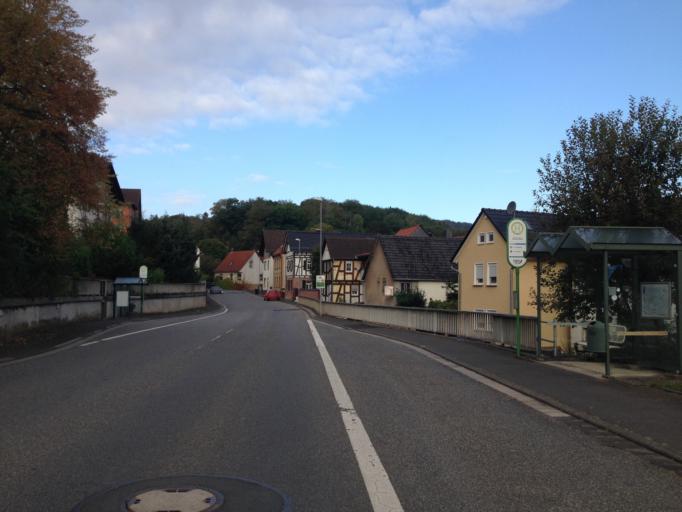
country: DE
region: Hesse
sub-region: Regierungsbezirk Giessen
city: Heuchelheim
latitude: 50.6262
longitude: 8.5811
